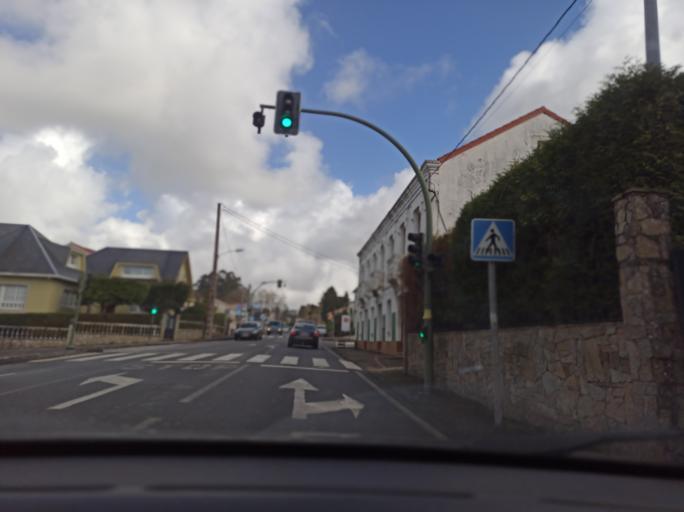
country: ES
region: Galicia
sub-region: Provincia da Coruna
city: Oleiros
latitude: 43.3329
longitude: -8.3114
